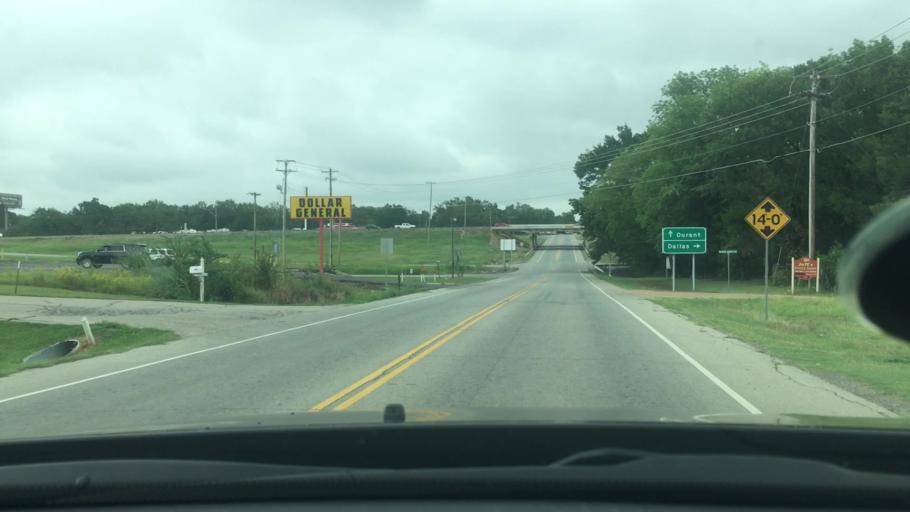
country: US
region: Oklahoma
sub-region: Bryan County
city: Colbert
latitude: 33.8530
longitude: -96.5146
